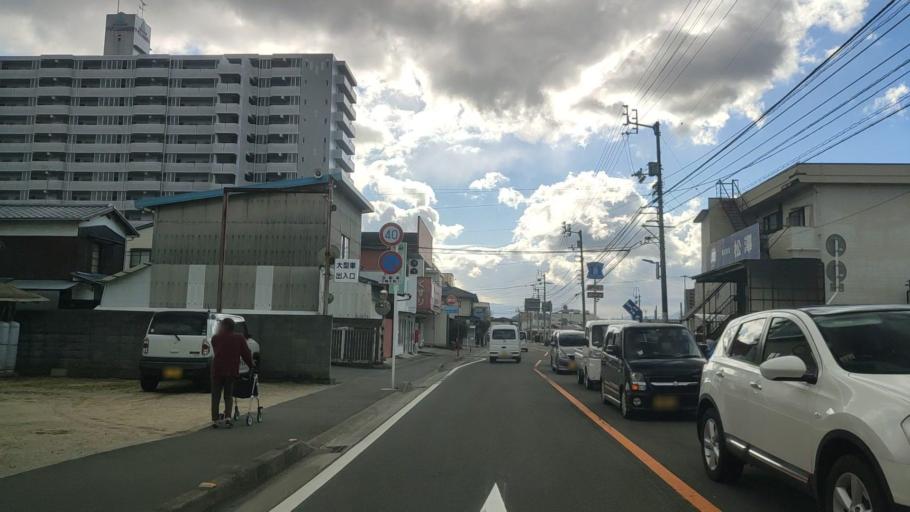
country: JP
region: Ehime
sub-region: Shikoku-chuo Shi
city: Matsuyama
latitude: 33.8675
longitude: 132.7183
